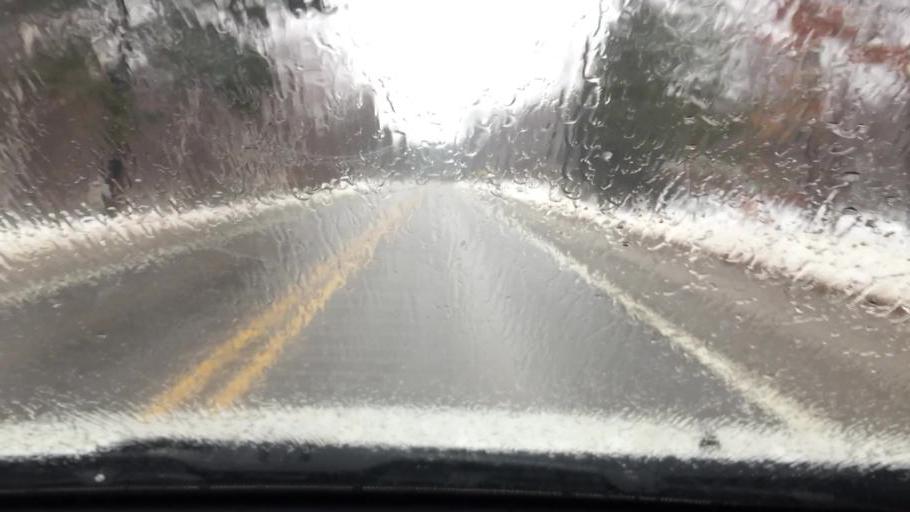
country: US
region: Michigan
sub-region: Charlevoix County
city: East Jordan
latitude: 45.2250
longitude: -85.1790
